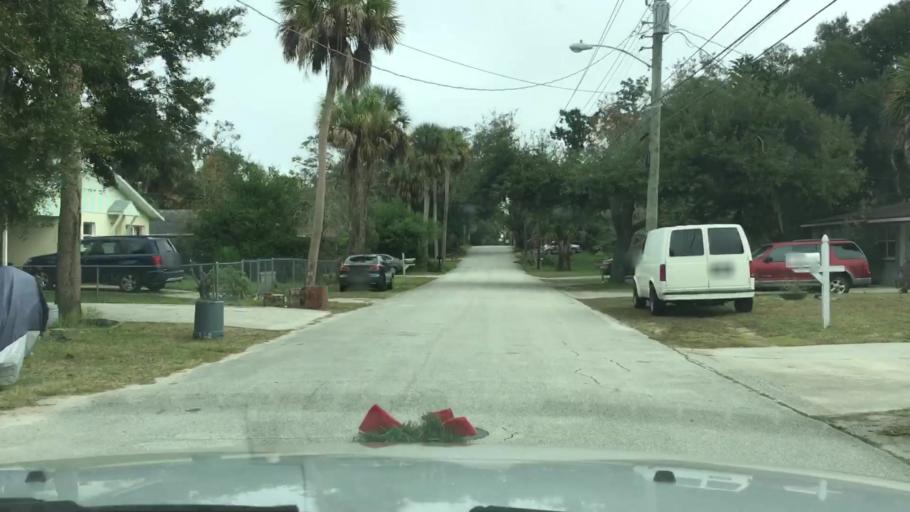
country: US
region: Florida
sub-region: Volusia County
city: Ormond Beach
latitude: 29.2869
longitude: -81.0615
